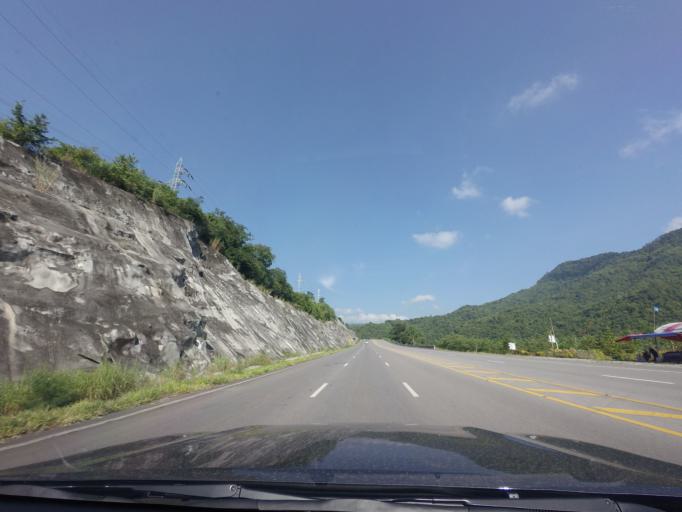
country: TH
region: Phetchabun
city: Lom Sak
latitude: 16.7714
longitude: 101.1346
